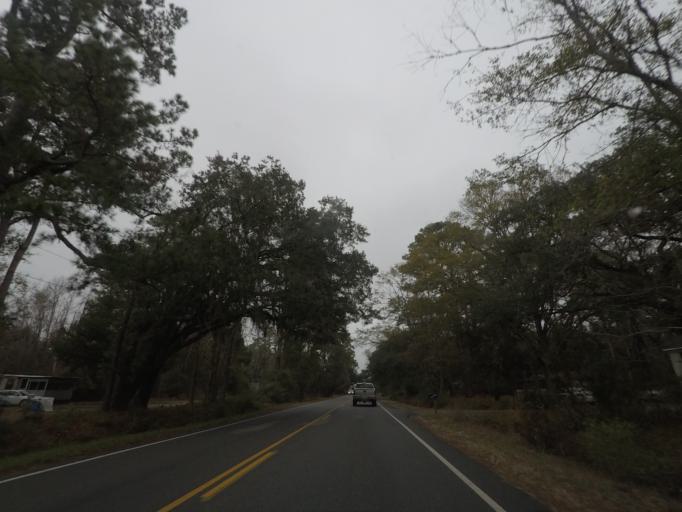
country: US
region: South Carolina
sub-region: Charleston County
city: Meggett
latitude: 32.6068
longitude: -80.3453
